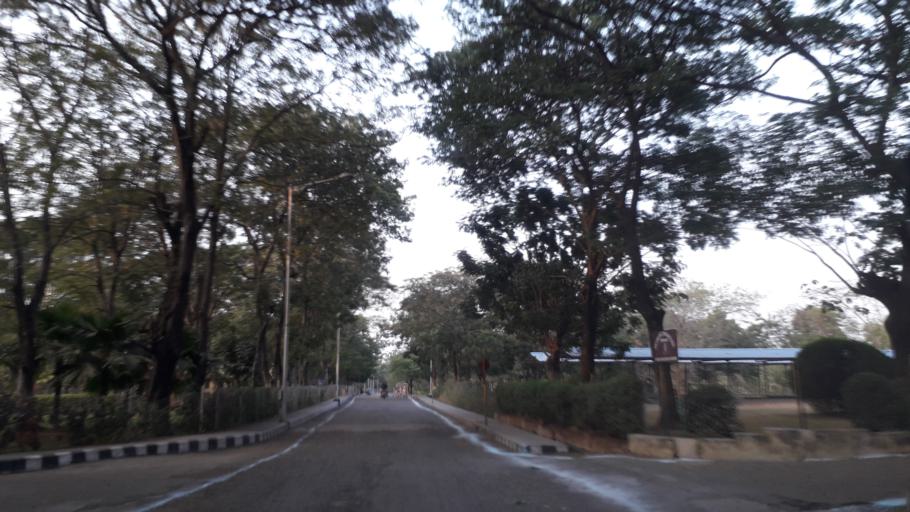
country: IN
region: Telangana
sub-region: Rangareddi
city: Singapur
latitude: 17.4680
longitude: 78.1647
